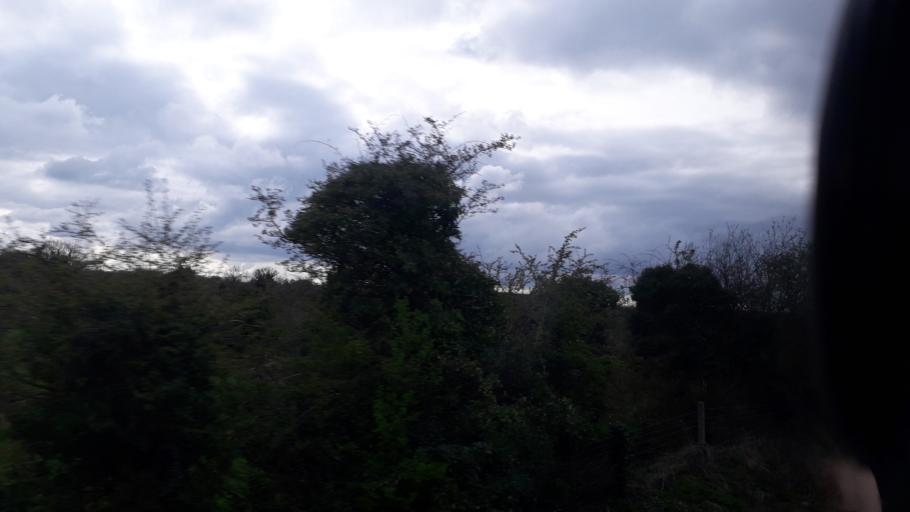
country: IE
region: Leinster
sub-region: An Longfort
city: Longford
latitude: 53.7094
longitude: -7.7301
